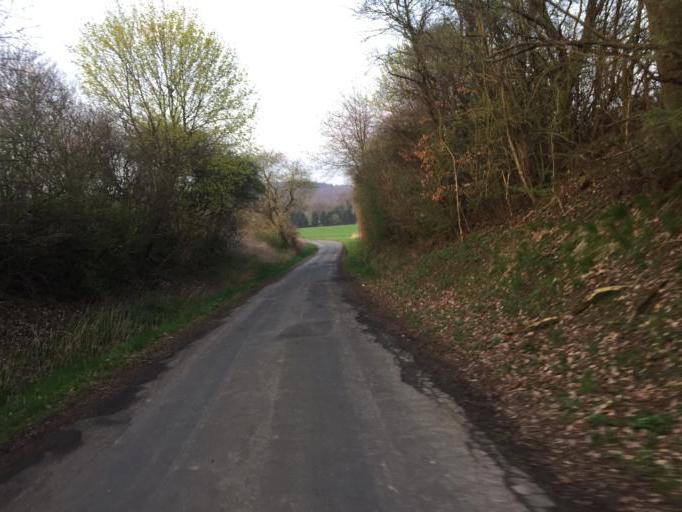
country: DE
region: Hesse
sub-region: Regierungsbezirk Giessen
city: Laubach
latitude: 50.5463
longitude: 9.0038
